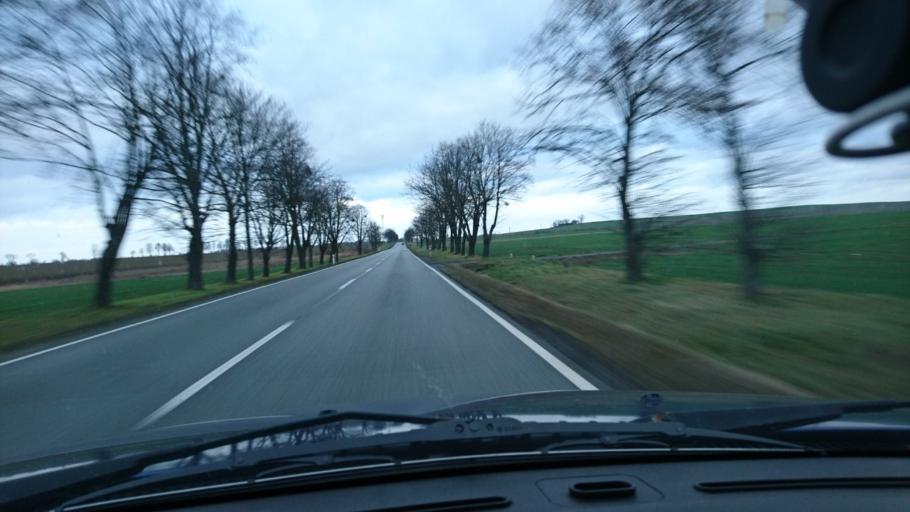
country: PL
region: Opole Voivodeship
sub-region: Powiat kluczborski
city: Byczyna
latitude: 51.0893
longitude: 18.2003
